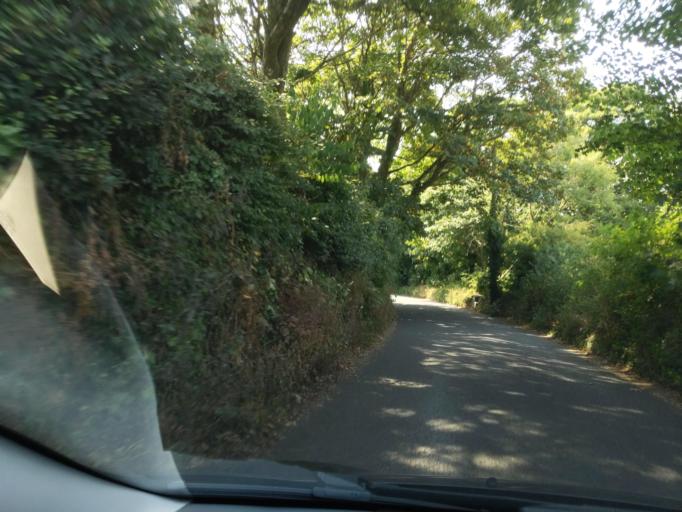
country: GB
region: England
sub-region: Cornwall
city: Fowey
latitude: 50.3430
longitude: -4.6276
